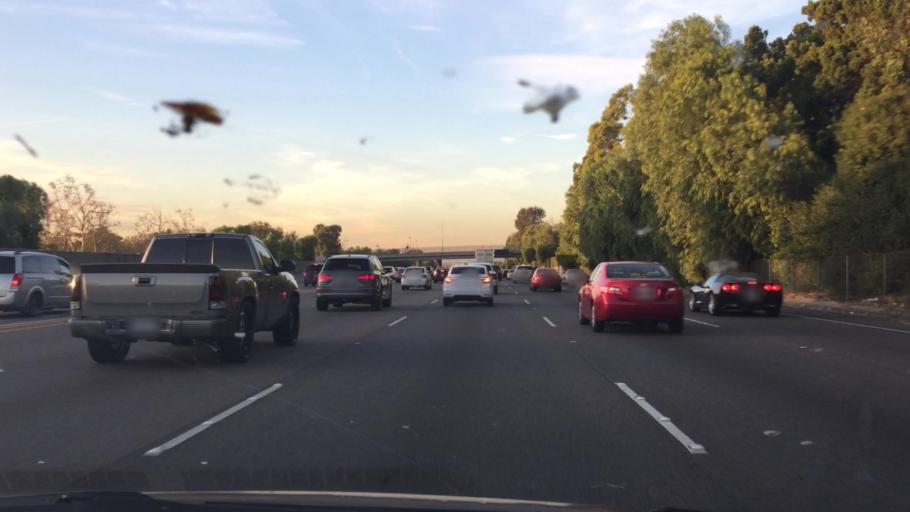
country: US
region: California
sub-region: Orange County
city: Irvine
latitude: 33.6980
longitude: -117.7735
